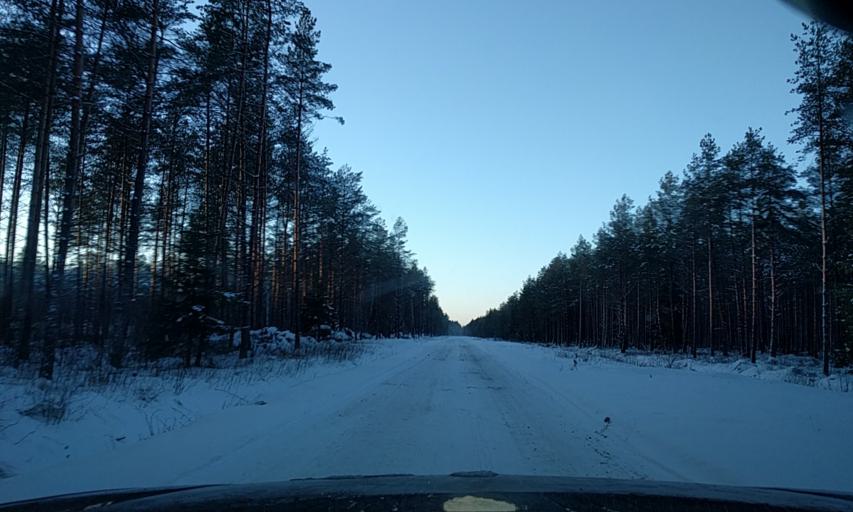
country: EE
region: Harju
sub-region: Saku vald
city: Saku
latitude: 59.3194
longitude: 24.6790
